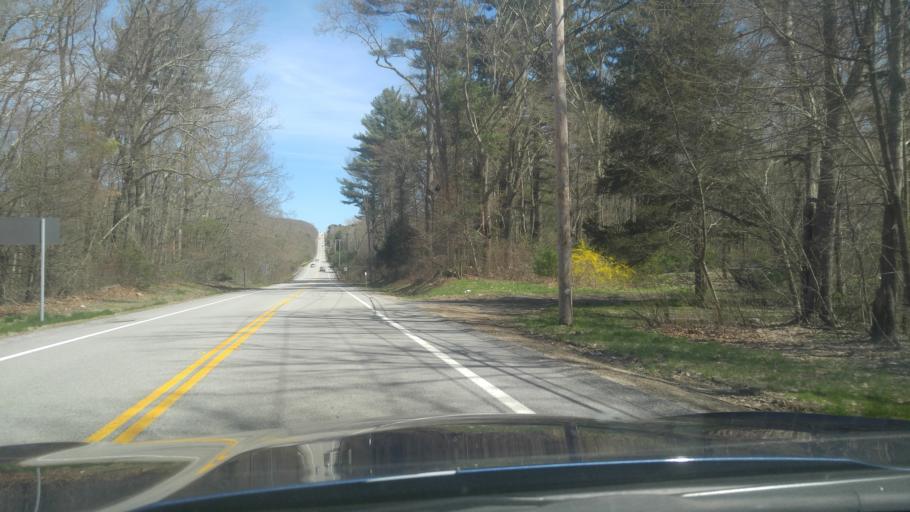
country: US
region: Rhode Island
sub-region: Washington County
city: Hope Valley
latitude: 41.5762
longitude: -71.7542
